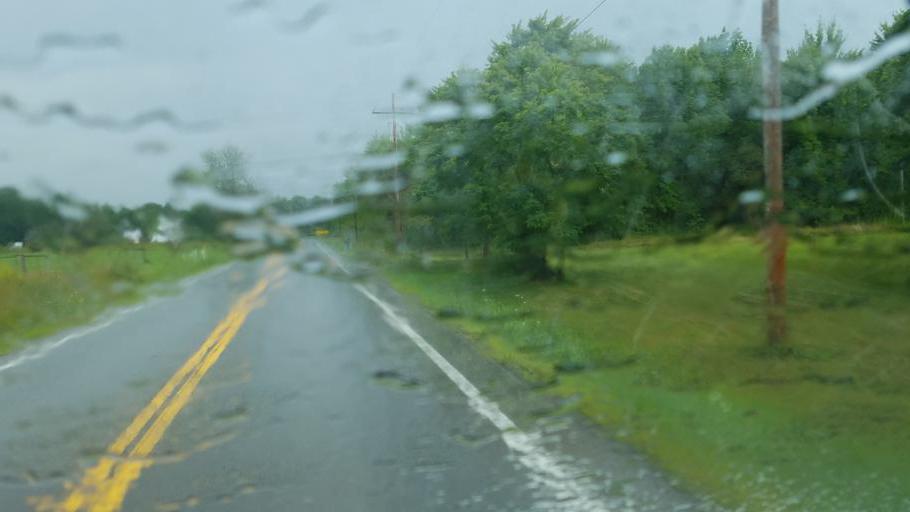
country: US
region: Ohio
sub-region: Ashtabula County
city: Orwell
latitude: 41.5545
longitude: -80.9506
